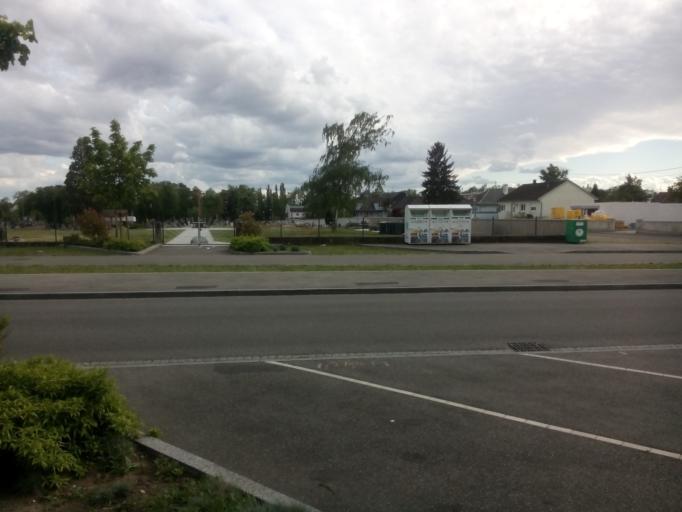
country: FR
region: Alsace
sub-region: Departement du Bas-Rhin
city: Bischwiller
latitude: 48.7755
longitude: 7.8479
